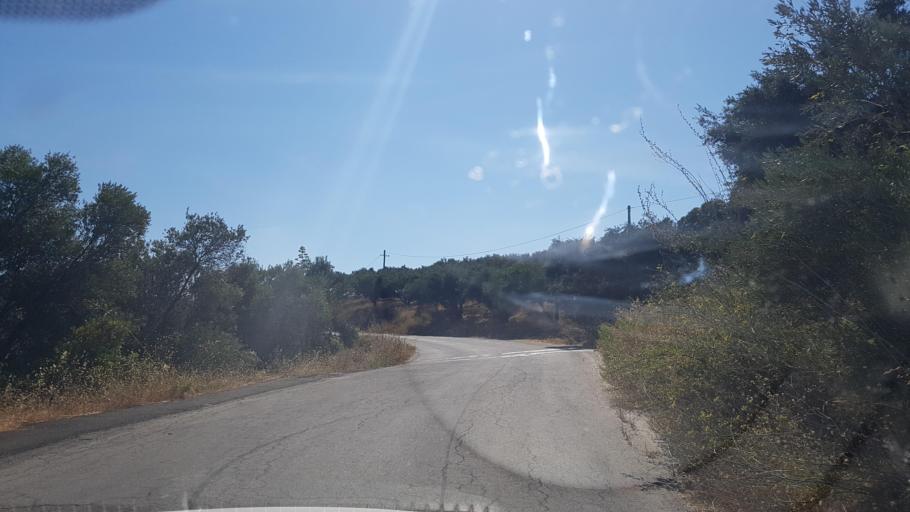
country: GR
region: Crete
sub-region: Nomos Chanias
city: Kissamos
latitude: 35.4982
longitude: 23.7226
